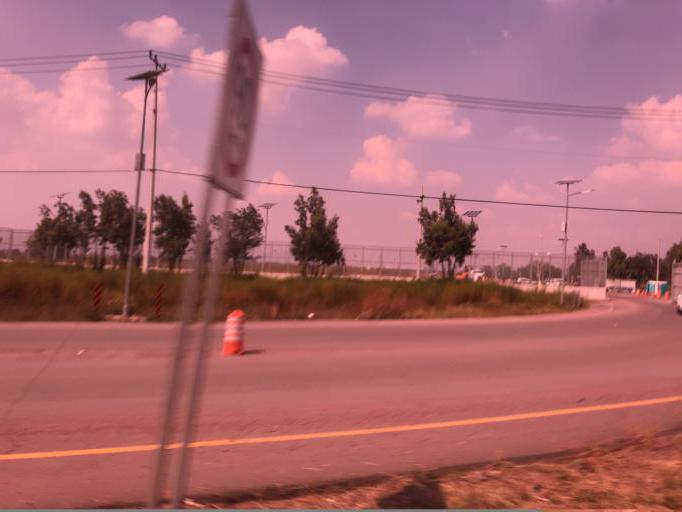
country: MX
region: Mexico
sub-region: Ciudad Nezahualcoyotl
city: Colonia Gustavo Baz Prada
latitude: 19.4718
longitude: -98.9983
